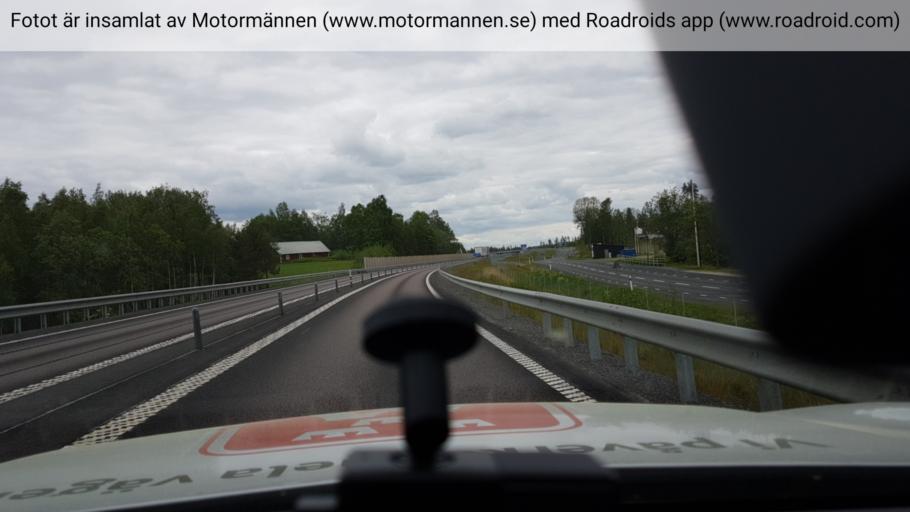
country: SE
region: Joenkoeping
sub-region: Habo Kommun
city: Habo
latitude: 57.8539
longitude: 14.0241
